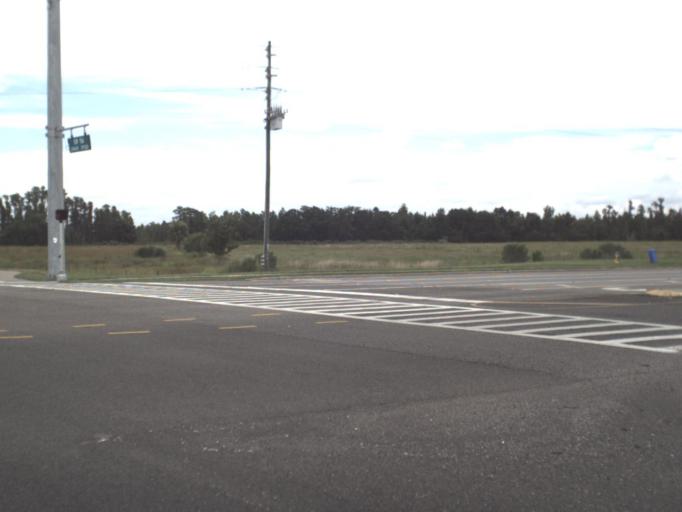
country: US
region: Florida
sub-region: Pasco County
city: Wesley Chapel
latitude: 28.1981
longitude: -82.3304
